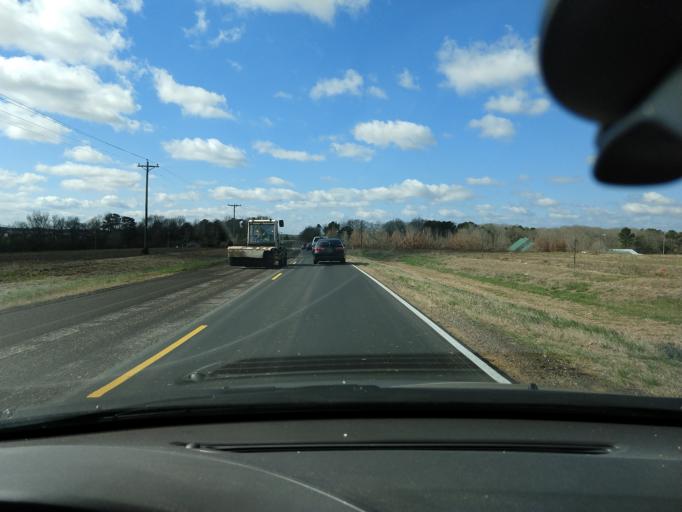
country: US
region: Alabama
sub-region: Coffee County
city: Elba
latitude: 31.2984
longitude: -86.0643
